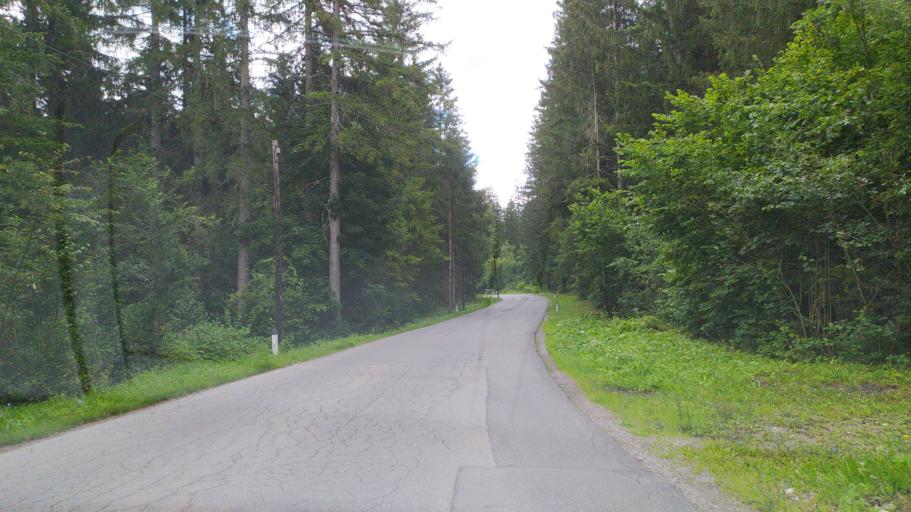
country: AT
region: Tyrol
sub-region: Politischer Bezirk Lienz
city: Tristach
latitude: 46.8138
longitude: 12.8142
